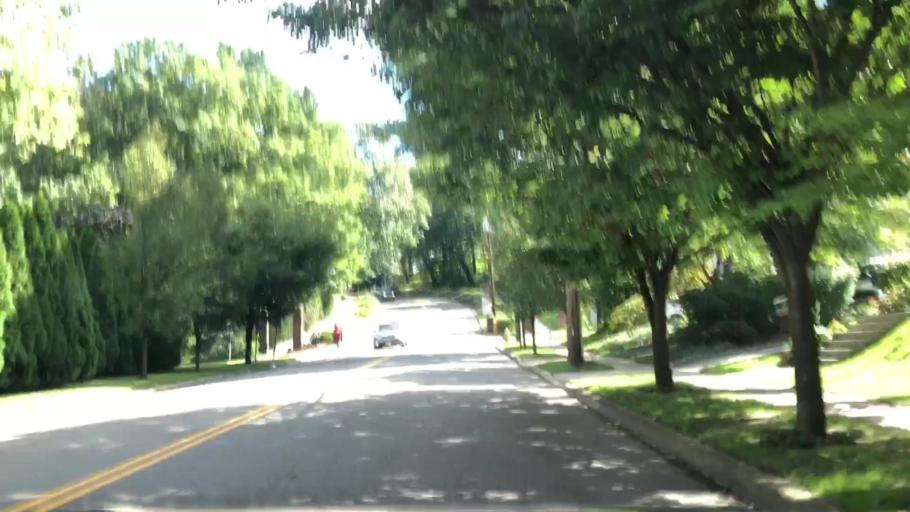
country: US
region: New York
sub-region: Nassau County
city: Manhasset
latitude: 40.7977
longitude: -73.6939
